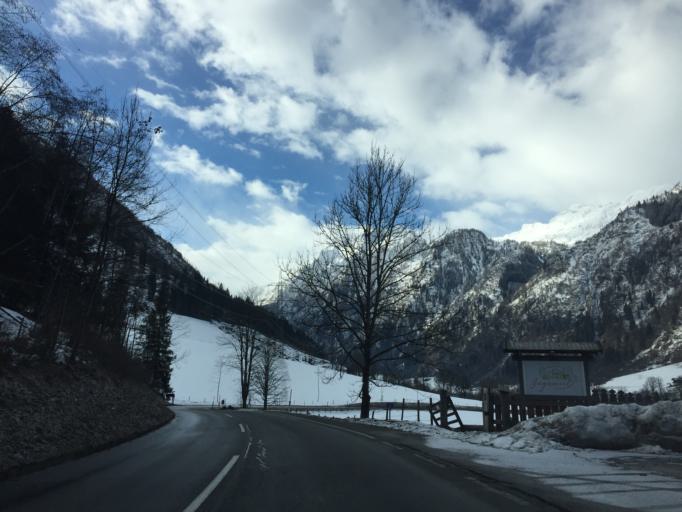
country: AT
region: Salzburg
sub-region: Politischer Bezirk Zell am See
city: Kaprun
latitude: 47.2548
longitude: 12.7433
